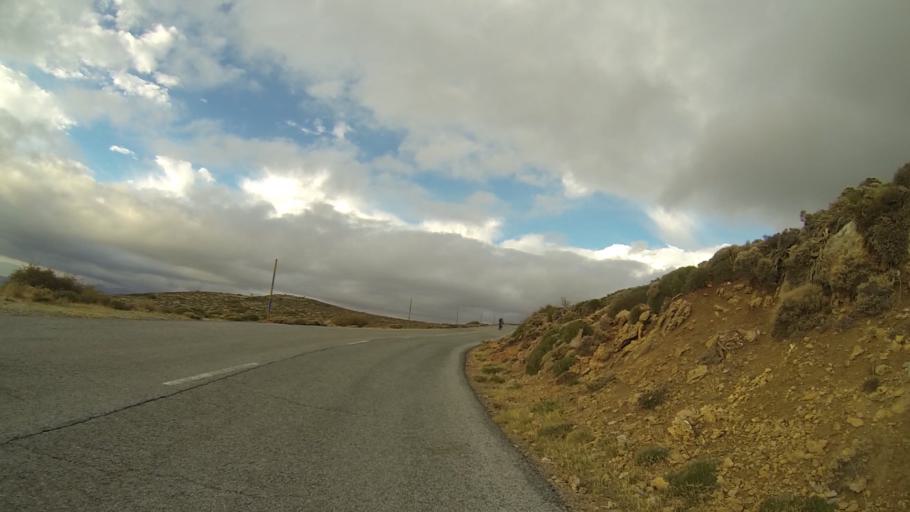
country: ES
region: Andalusia
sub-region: Provincia de Granada
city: Guejar-Sierra
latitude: 37.1213
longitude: -3.4322
